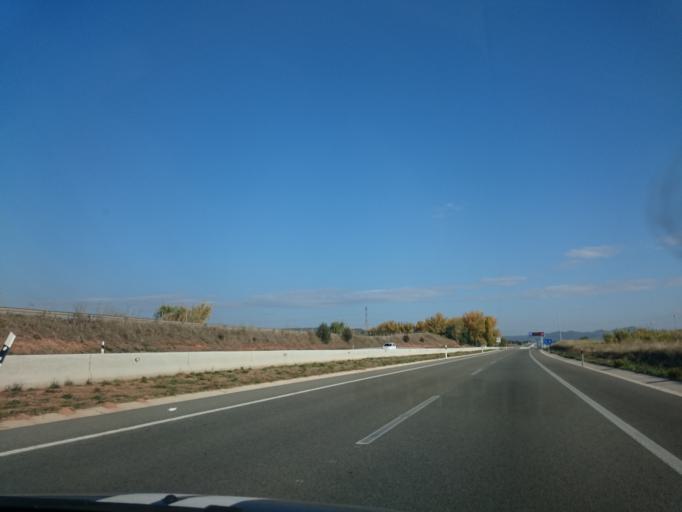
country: ES
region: Catalonia
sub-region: Provincia de Barcelona
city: Sant Fruitos de Bages
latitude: 41.7652
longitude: 1.8688
